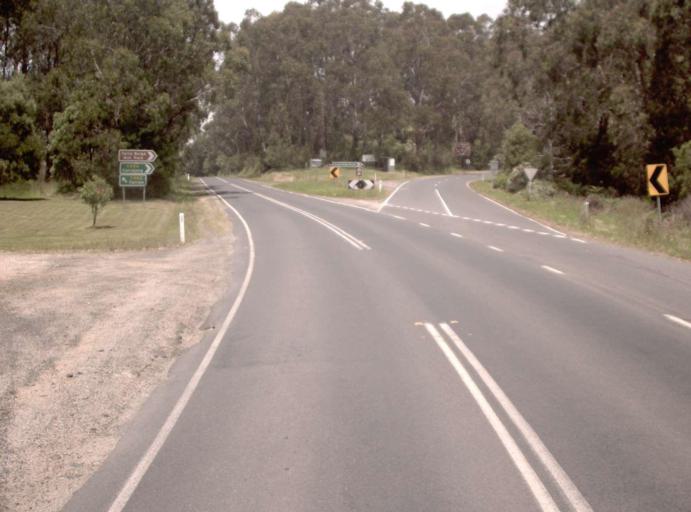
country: AU
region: Victoria
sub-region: Latrobe
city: Traralgon
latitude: -38.3491
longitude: 146.7147
